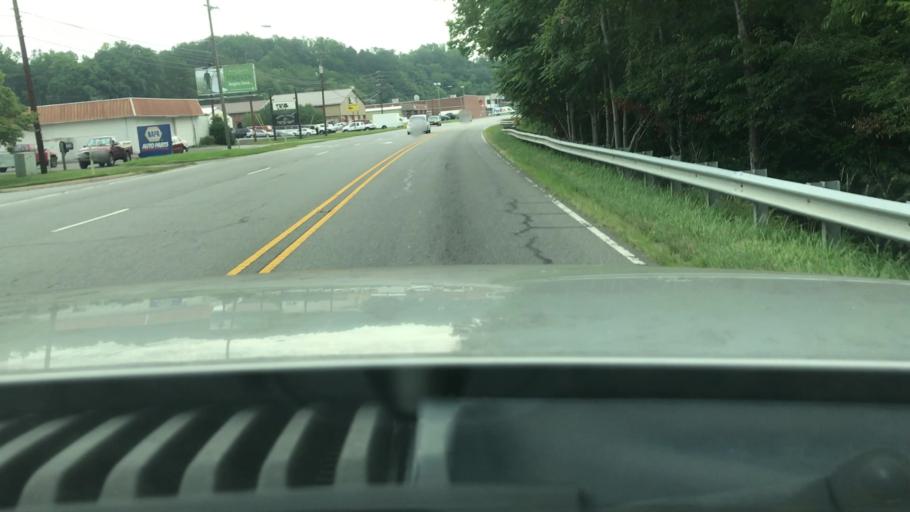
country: US
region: North Carolina
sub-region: Wilkes County
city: Wilkesboro
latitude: 36.1546
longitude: -81.1718
